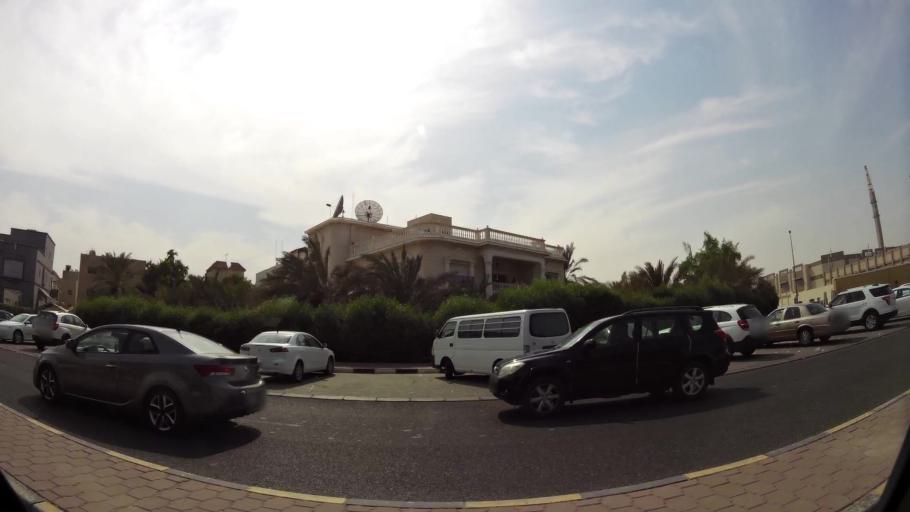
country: KW
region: Al Asimah
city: Ash Shamiyah
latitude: 29.3393
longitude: 47.9534
